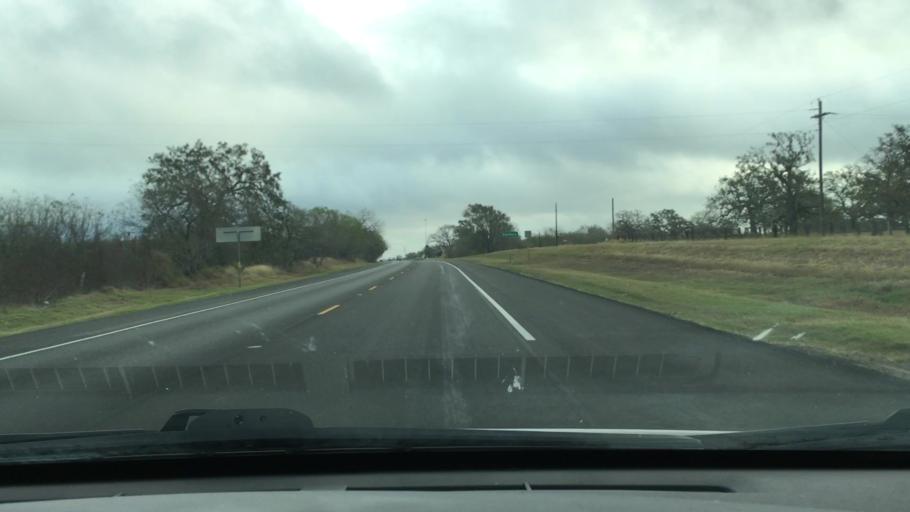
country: US
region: Texas
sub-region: Gonzales County
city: Nixon
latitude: 29.2489
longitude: -97.8445
